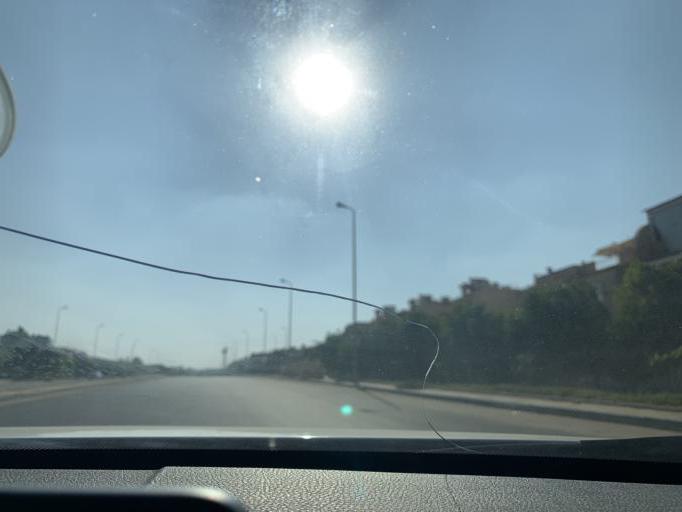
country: EG
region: Muhafazat al Qalyubiyah
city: Al Khankah
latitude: 30.0111
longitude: 31.4849
